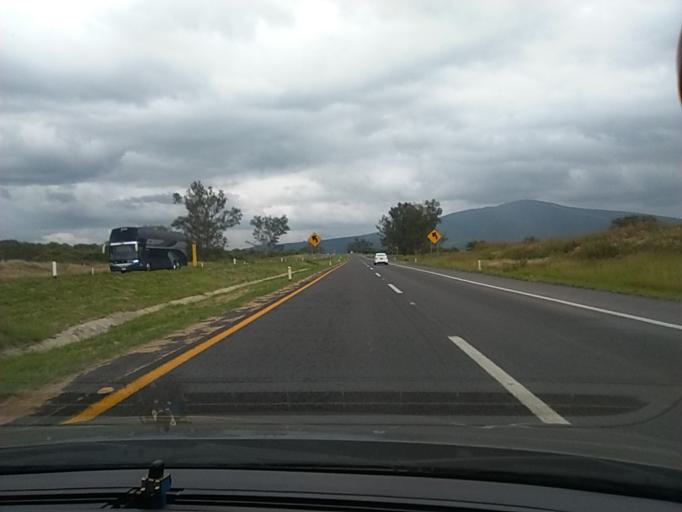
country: MX
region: Jalisco
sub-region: Zapotlanejo
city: La Mezquitera
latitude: 20.5723
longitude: -103.0848
